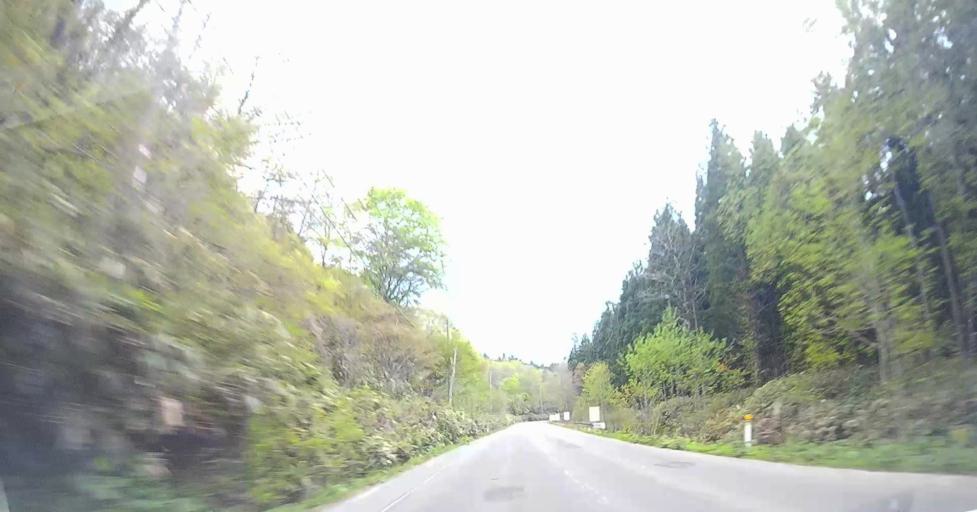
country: JP
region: Aomori
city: Goshogawara
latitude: 41.1163
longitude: 140.5271
